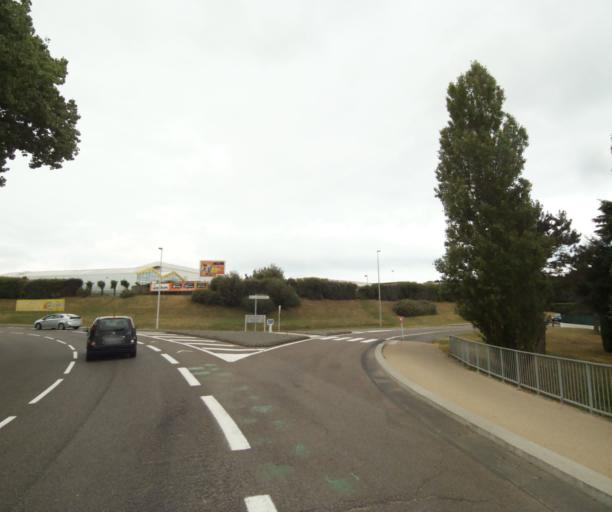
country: FR
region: Pays de la Loire
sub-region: Departement de la Vendee
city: Chateau-d'Olonne
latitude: 46.4888
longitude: -1.7502
